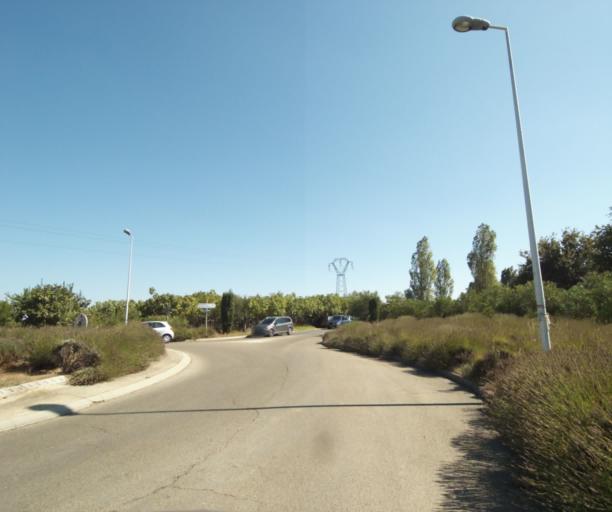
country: FR
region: Languedoc-Roussillon
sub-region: Departement du Gard
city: Bouillargues
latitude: 43.8057
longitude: 4.4269
